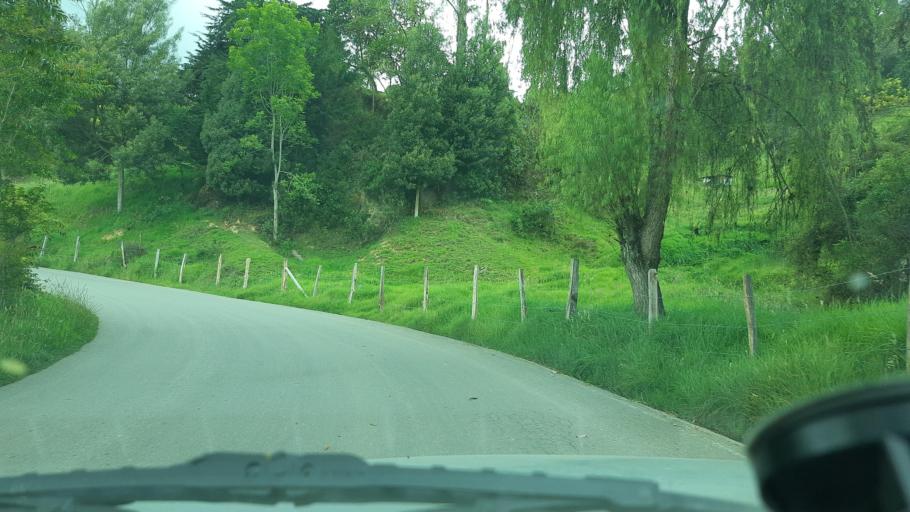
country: CO
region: Cundinamarca
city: Umbita
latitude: 5.2220
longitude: -73.4617
